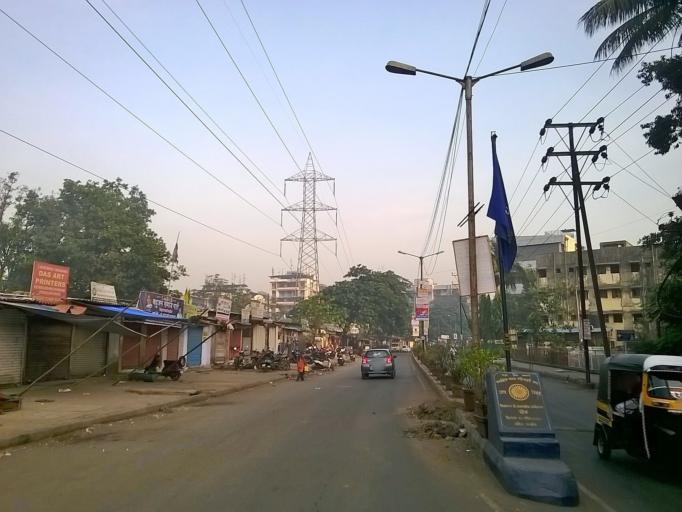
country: IN
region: Maharashtra
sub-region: Raigarh
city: Panvel
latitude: 18.9934
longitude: 73.1208
